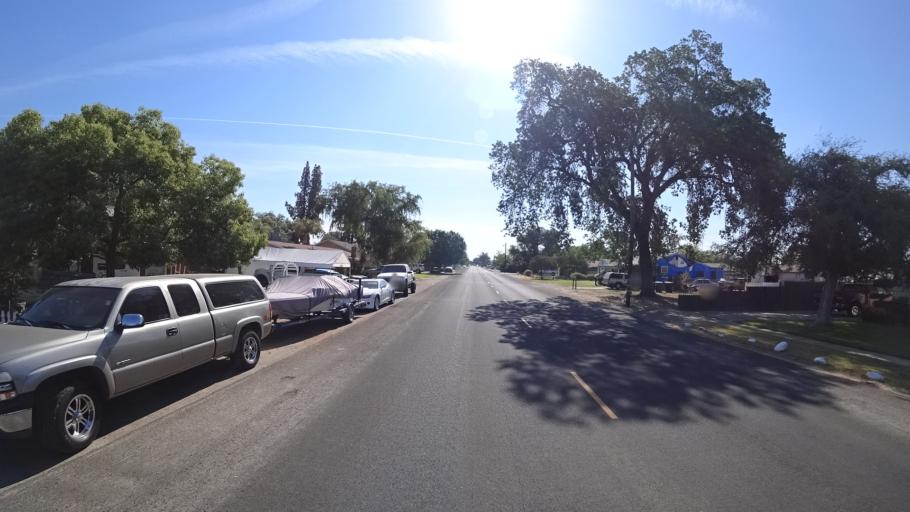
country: US
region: California
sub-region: Kings County
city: Hanford
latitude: 36.3331
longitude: -119.6356
